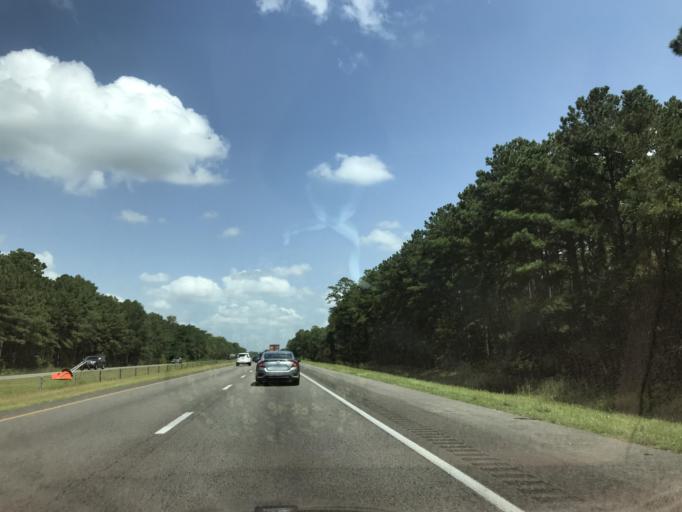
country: US
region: North Carolina
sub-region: New Hanover County
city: Castle Hayne
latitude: 34.3789
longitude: -77.8822
